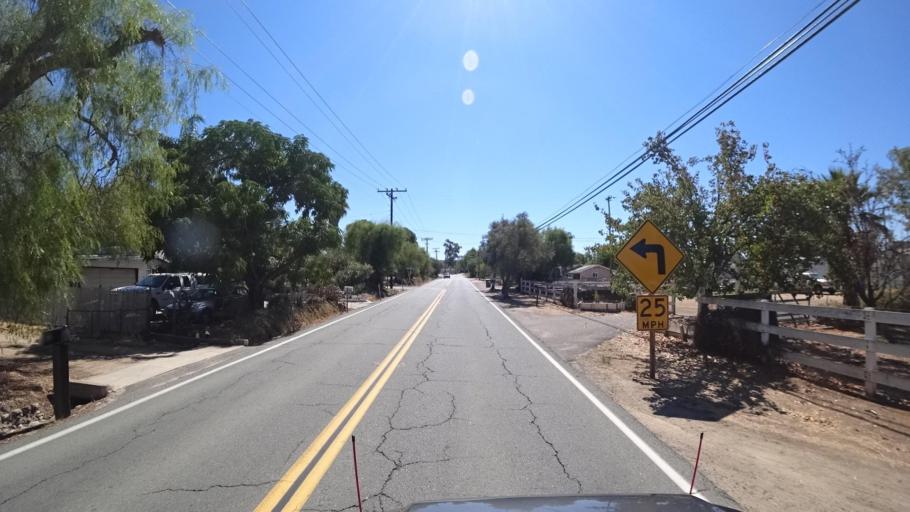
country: US
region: California
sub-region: San Diego County
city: Ramona
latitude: 33.0418
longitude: -116.8527
